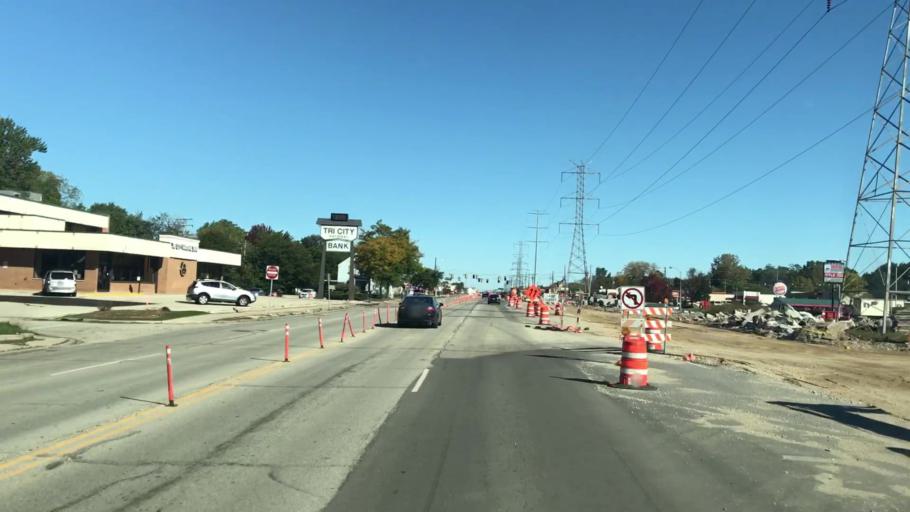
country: US
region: Wisconsin
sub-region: Milwaukee County
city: Hales Corners
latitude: 42.9421
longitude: -88.0484
